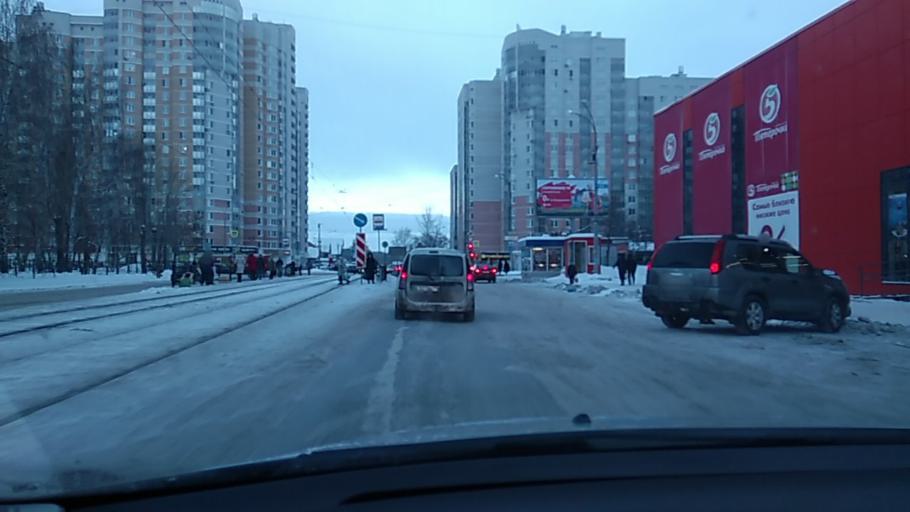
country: RU
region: Sverdlovsk
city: Yekaterinburg
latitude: 56.9034
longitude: 60.5877
